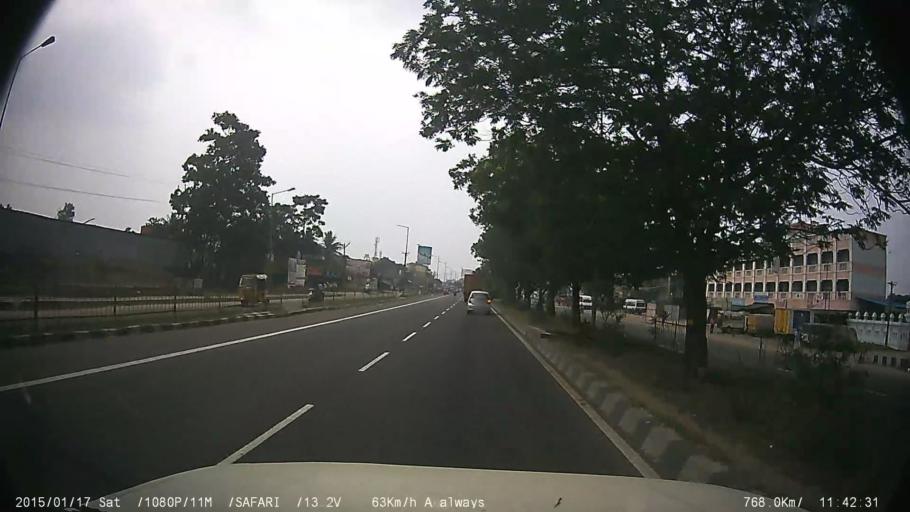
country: IN
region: Tamil Nadu
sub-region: Kancheepuram
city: Singapperumalkovil
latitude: 12.7654
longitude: 80.0051
